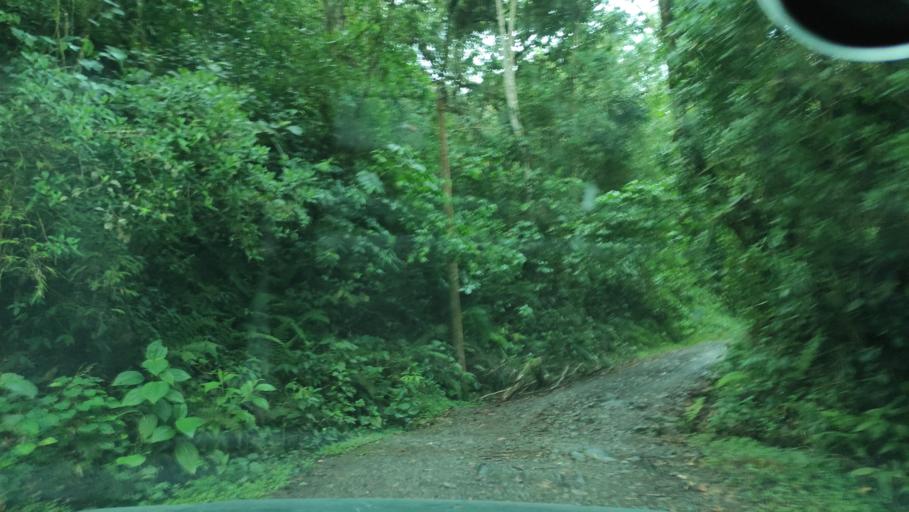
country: CO
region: Valle del Cauca
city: Jamundi
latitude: 3.3219
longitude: -76.6331
